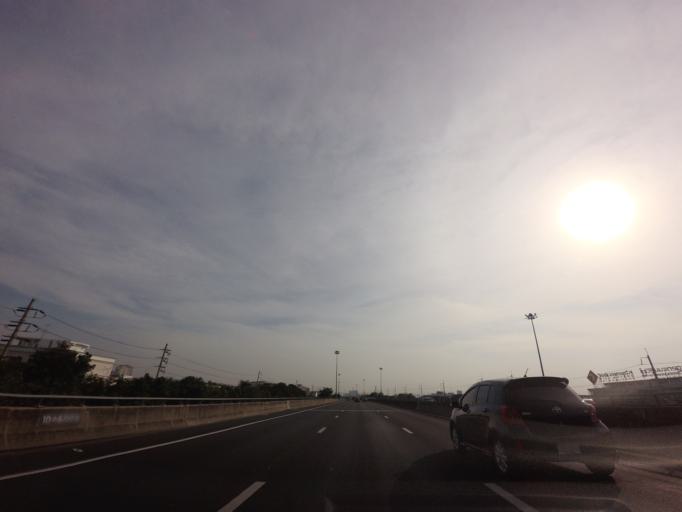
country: TH
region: Bangkok
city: Wang Thonglang
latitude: 13.7846
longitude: 100.6083
